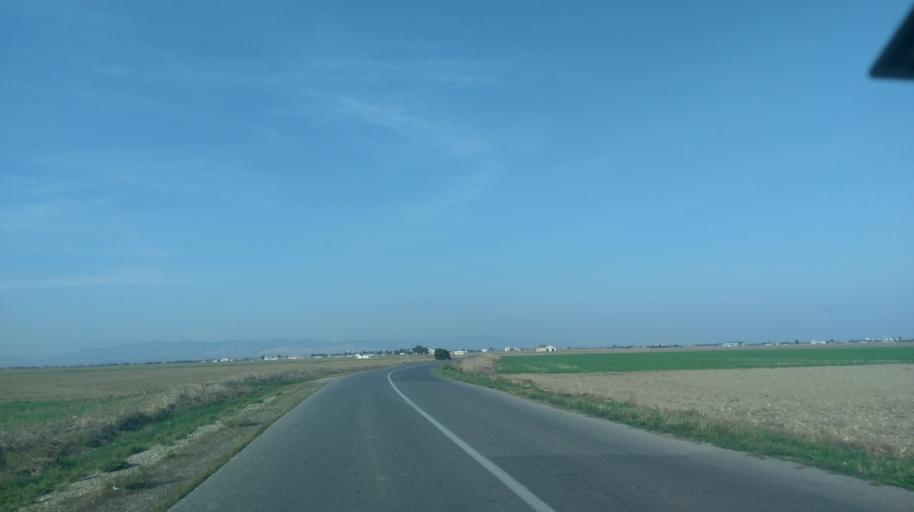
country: CY
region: Ammochostos
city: Achna
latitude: 35.1509
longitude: 33.7494
